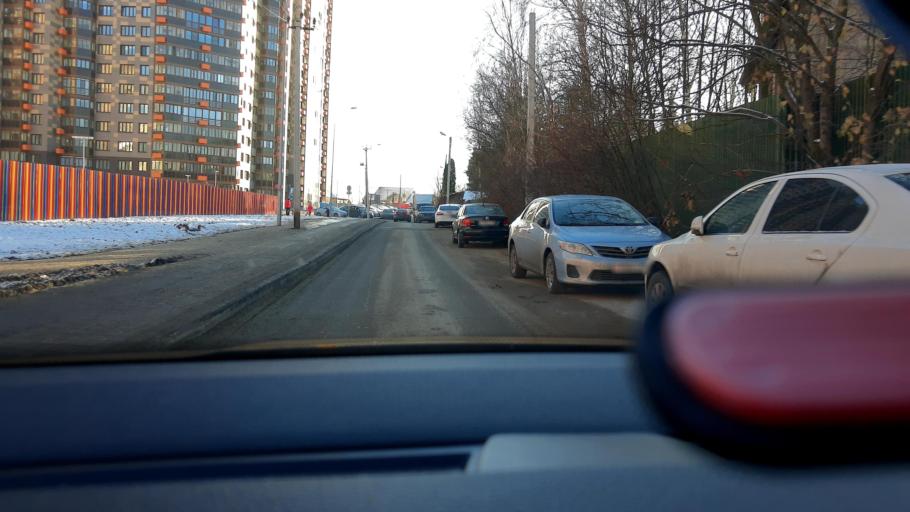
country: RU
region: Moskovskaya
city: Odintsovo
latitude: 55.6974
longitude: 37.3184
